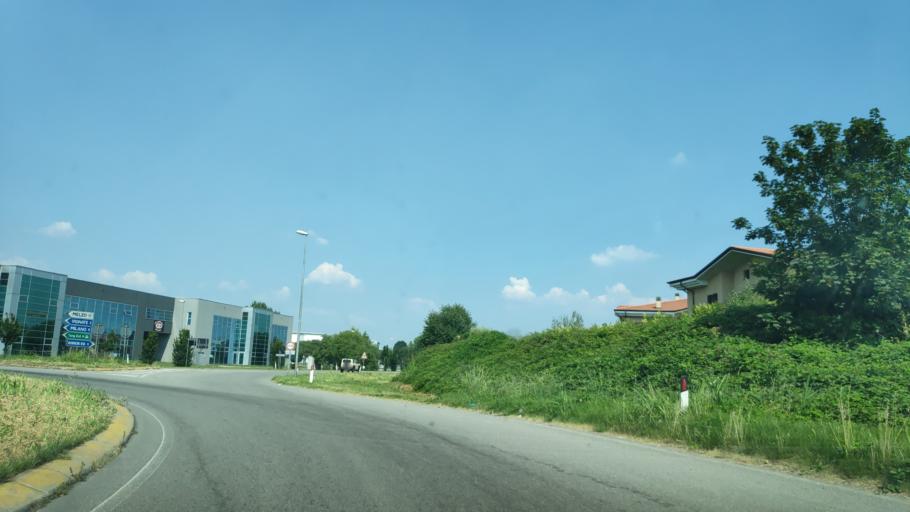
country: IT
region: Lombardy
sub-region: Citta metropolitana di Milano
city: Liscate
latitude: 45.4835
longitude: 9.4042
